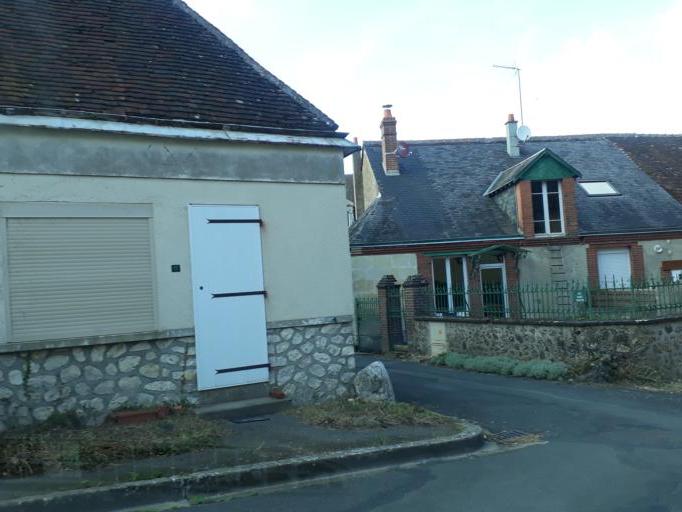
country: FR
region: Centre
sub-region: Departement du Loir-et-Cher
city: Aze
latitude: 47.8926
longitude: 1.0277
